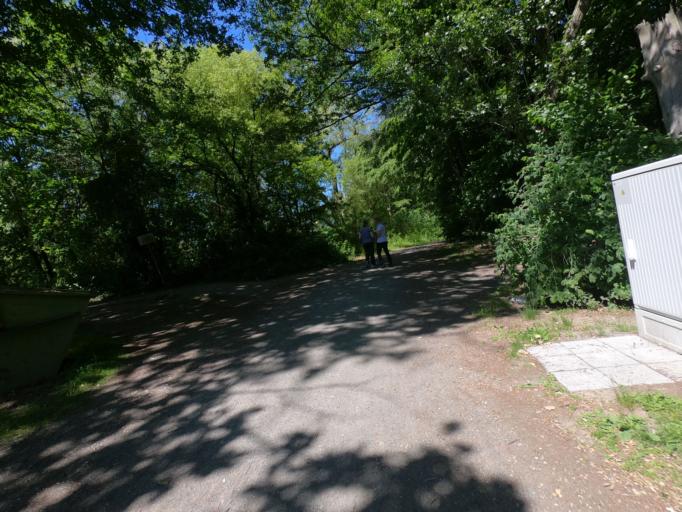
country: DE
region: Hesse
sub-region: Regierungsbezirk Darmstadt
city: Offenbach
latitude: 50.0618
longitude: 8.7519
